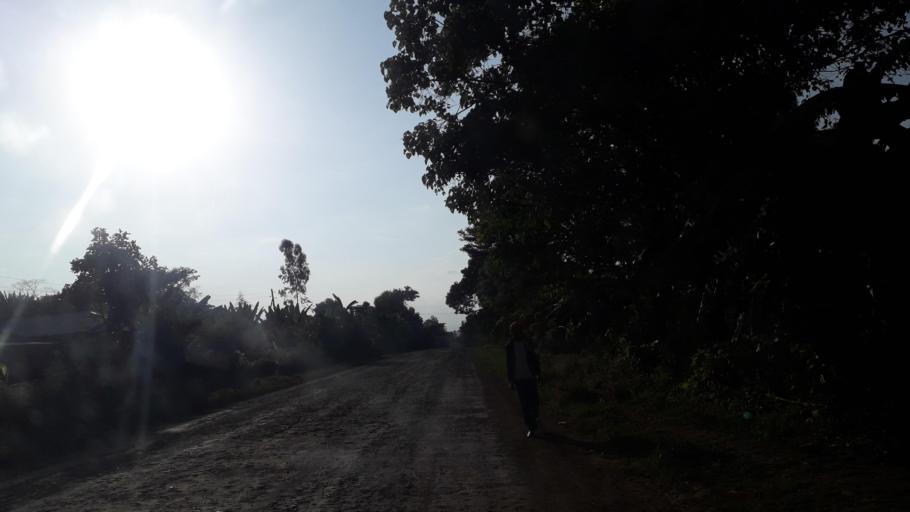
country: ET
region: Oromiya
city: Jima
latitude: 7.5462
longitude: 36.8730
